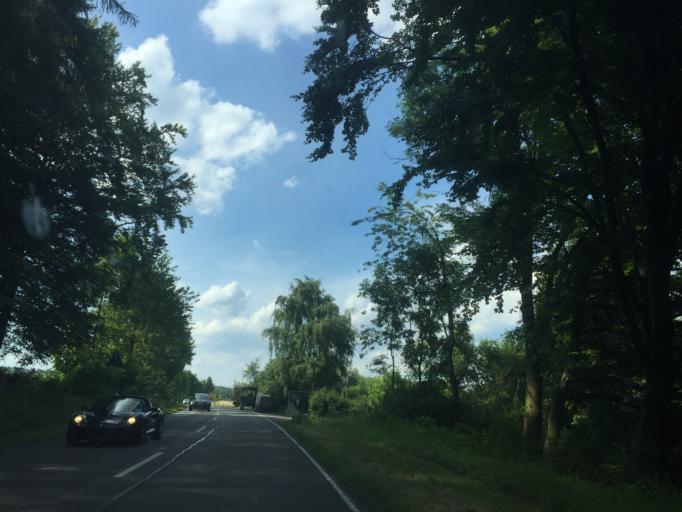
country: DE
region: Baden-Wuerttemberg
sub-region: Karlsruhe Region
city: Gaiberg
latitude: 49.3576
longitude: 8.7441
